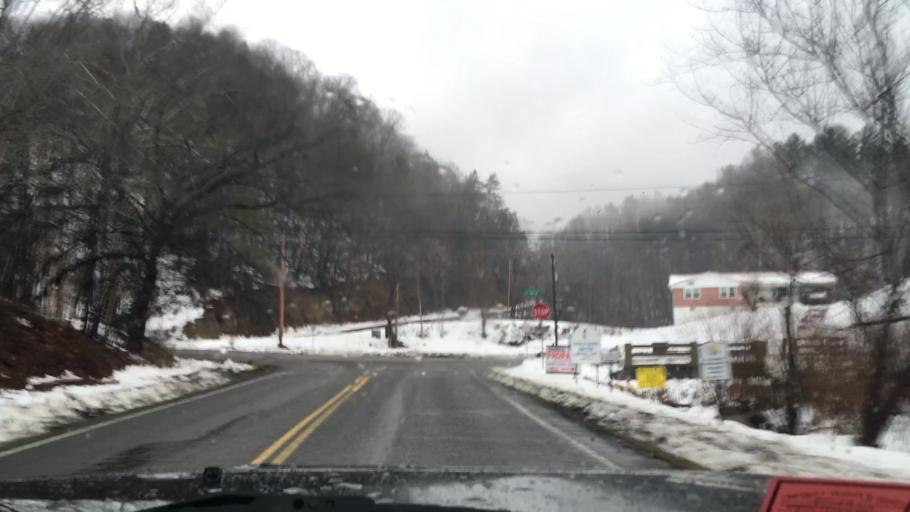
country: US
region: Virginia
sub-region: Pulaski County
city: Dublin
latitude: 37.0011
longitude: -80.6768
